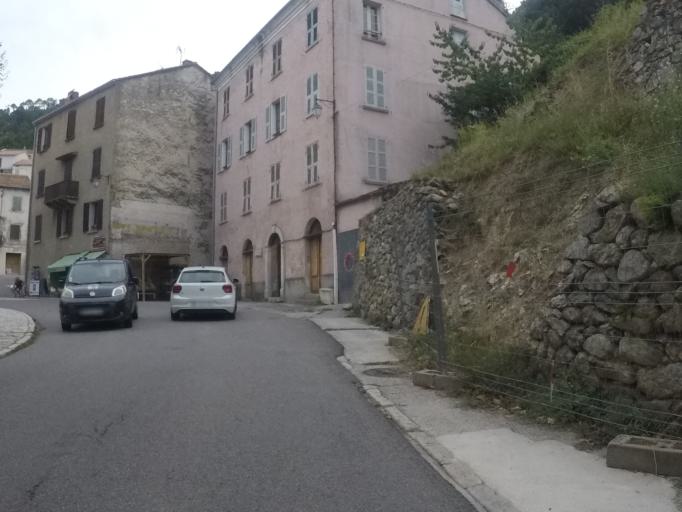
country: FR
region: Corsica
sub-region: Departement de la Haute-Corse
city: Corte
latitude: 42.1729
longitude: 9.1692
